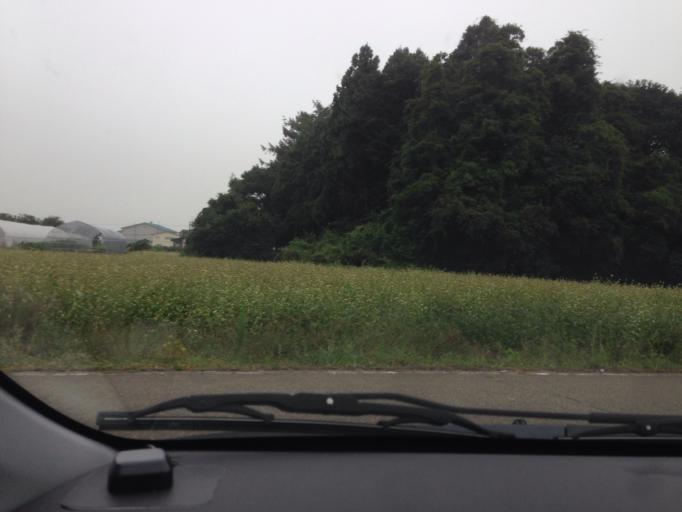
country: JP
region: Fukushima
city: Kitakata
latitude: 37.5640
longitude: 139.8691
